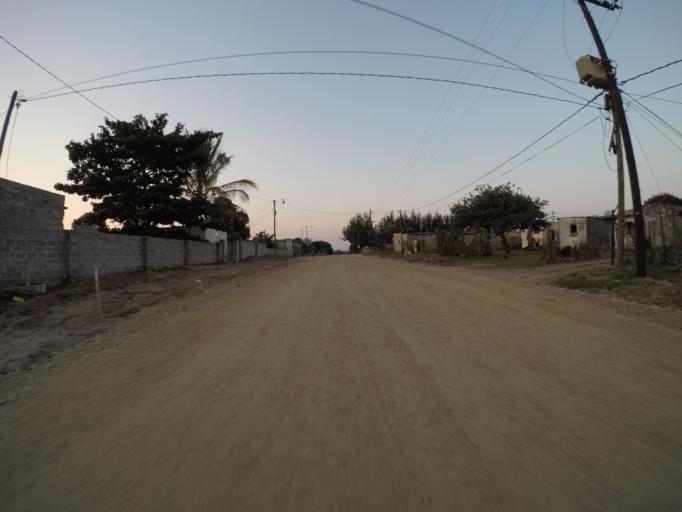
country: ZA
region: KwaZulu-Natal
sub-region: uThungulu District Municipality
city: Richards Bay
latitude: -28.7572
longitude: 32.1292
